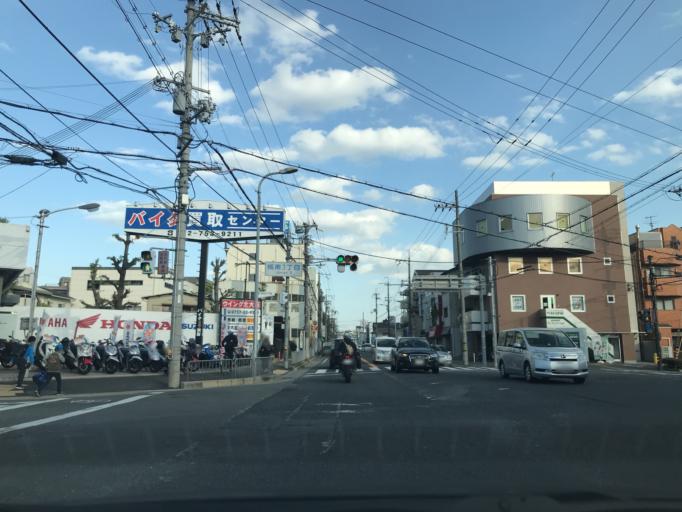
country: JP
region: Osaka
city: Ikeda
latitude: 34.8191
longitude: 135.4314
